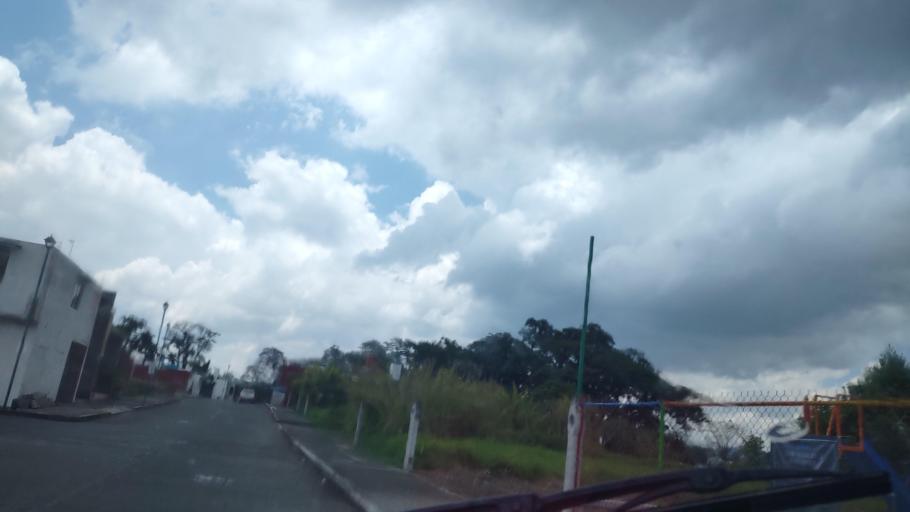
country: MX
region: Veracruz
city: Coatepec
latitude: 19.4462
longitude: -96.9495
